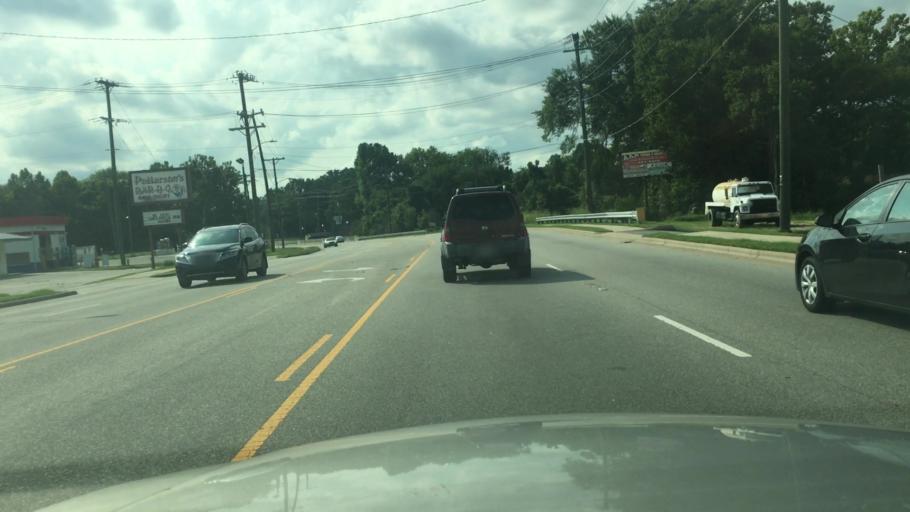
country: US
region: North Carolina
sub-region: Cumberland County
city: Fayetteville
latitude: 35.0462
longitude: -78.8530
